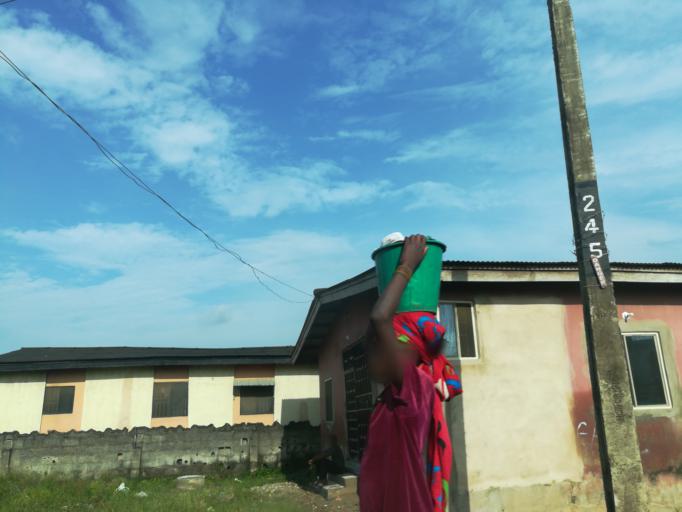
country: NG
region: Lagos
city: Ojota
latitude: 6.6034
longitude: 3.4221
